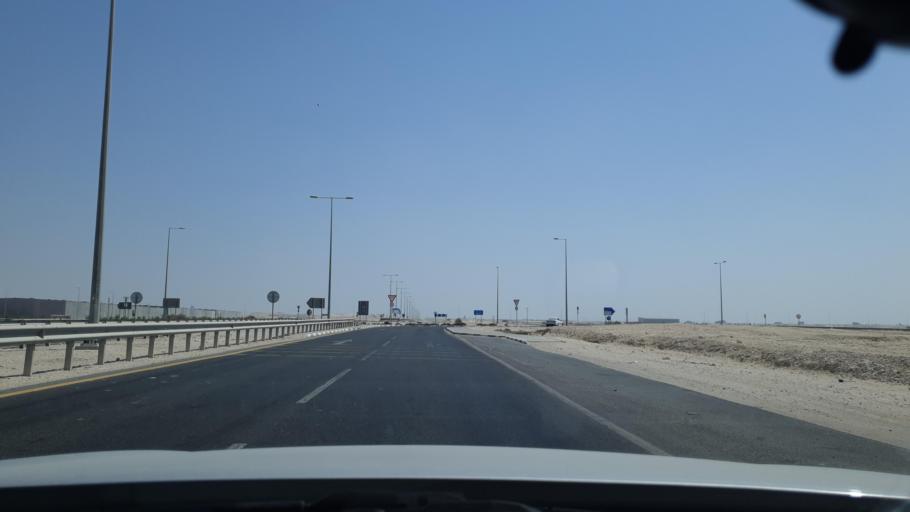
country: QA
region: Baladiyat Umm Salal
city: Umm Salal Muhammad
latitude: 25.3876
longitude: 51.3479
